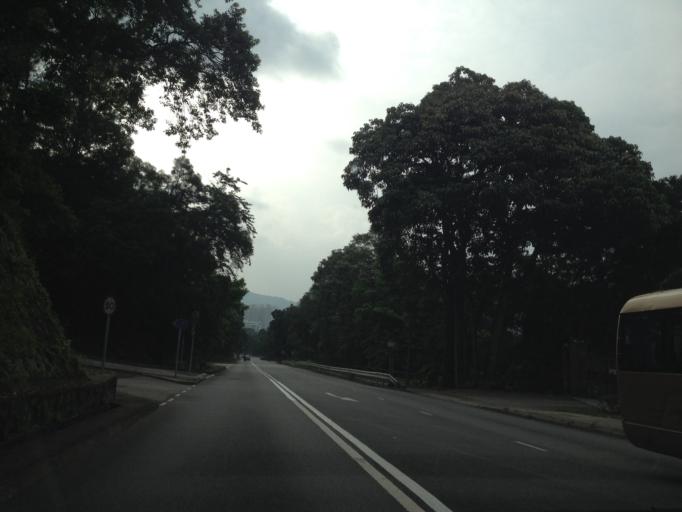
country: HK
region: Tai Po
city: Tai Po
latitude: 22.4399
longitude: 114.1824
